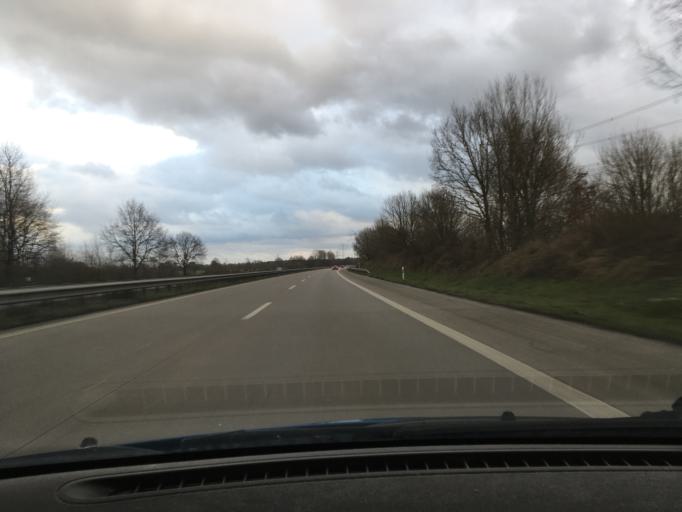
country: DE
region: Schleswig-Holstein
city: Klein Offenseth-Sparrieshoop
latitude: 53.7921
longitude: 9.6970
